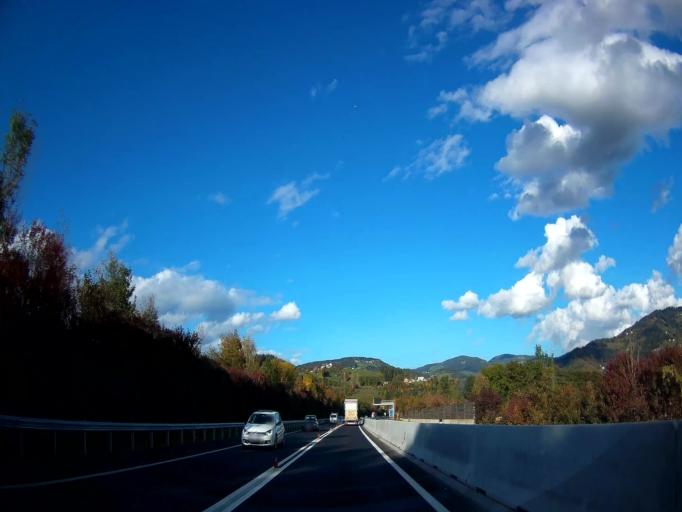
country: AT
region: Carinthia
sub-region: Politischer Bezirk Wolfsberg
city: Wolfsberg
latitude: 46.8383
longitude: 14.8218
